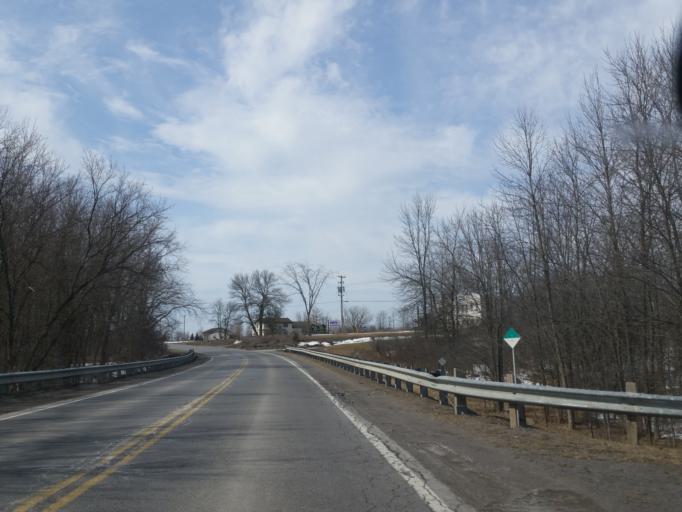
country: CA
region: Ontario
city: Deseronto
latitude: 44.1929
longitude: -77.1110
